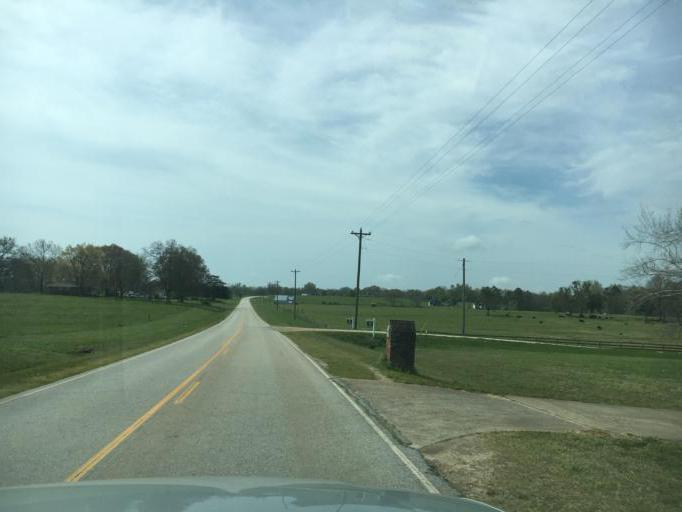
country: US
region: Georgia
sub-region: Franklin County
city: Lavonia
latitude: 34.4115
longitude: -83.0745
